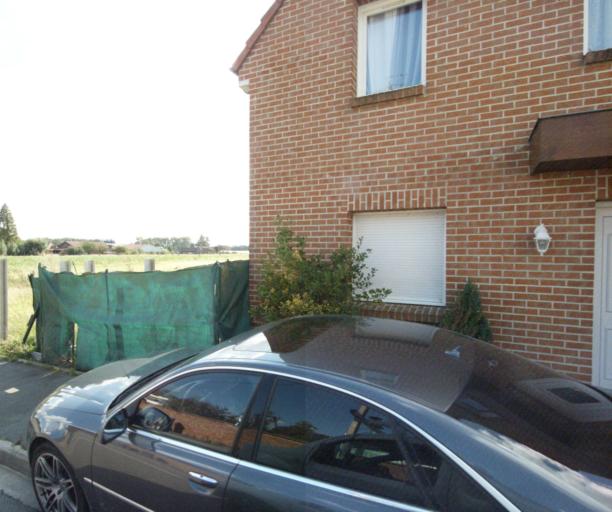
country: FR
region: Nord-Pas-de-Calais
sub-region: Departement du Nord
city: Herlies
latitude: 50.5718
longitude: 2.8638
